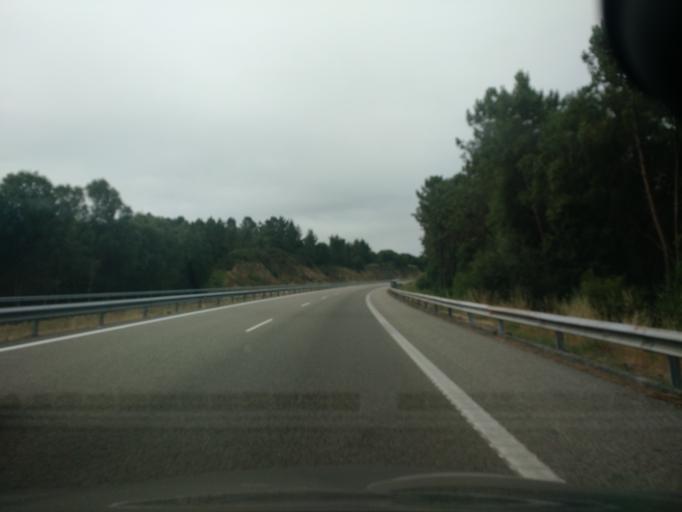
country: ES
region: Galicia
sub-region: Provincia da Coruna
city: Oroso
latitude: 42.9564
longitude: -8.4565
